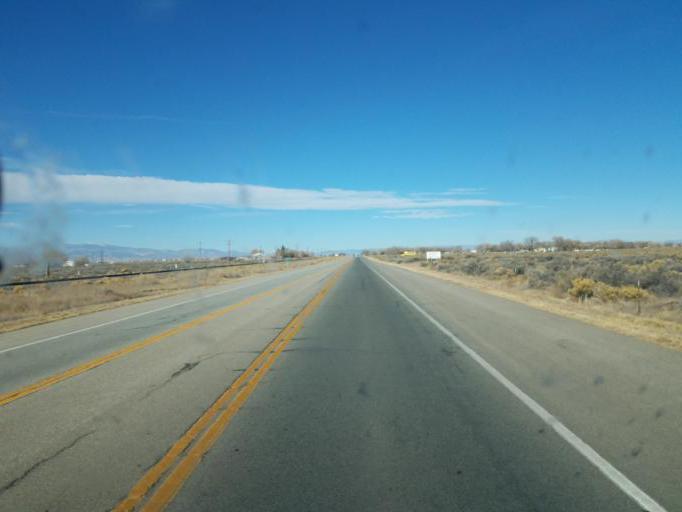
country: US
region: Colorado
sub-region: Alamosa County
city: Alamosa
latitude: 37.4917
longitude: -105.9336
